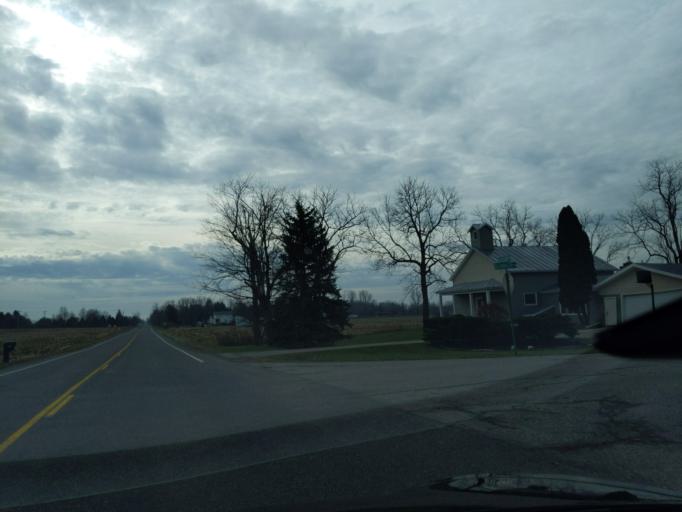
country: US
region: Michigan
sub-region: Ingham County
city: Mason
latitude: 42.5532
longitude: -84.5227
